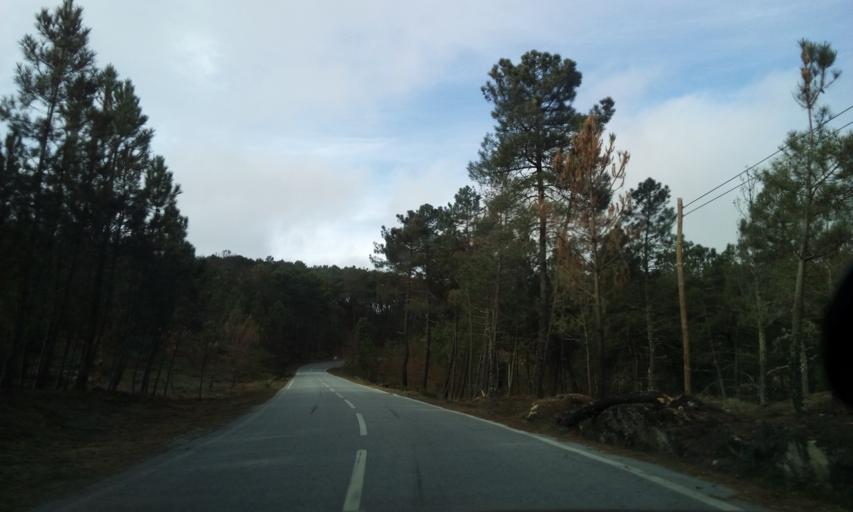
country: PT
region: Guarda
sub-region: Aguiar da Beira
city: Aguiar da Beira
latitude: 40.7691
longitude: -7.5298
